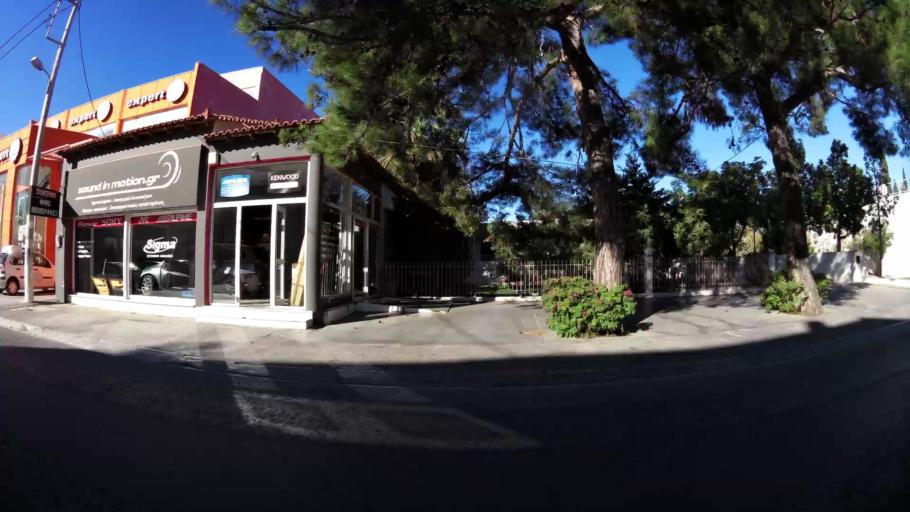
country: GR
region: Attica
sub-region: Nomarchia Anatolikis Attikis
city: Koropi
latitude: 37.9118
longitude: 23.8738
